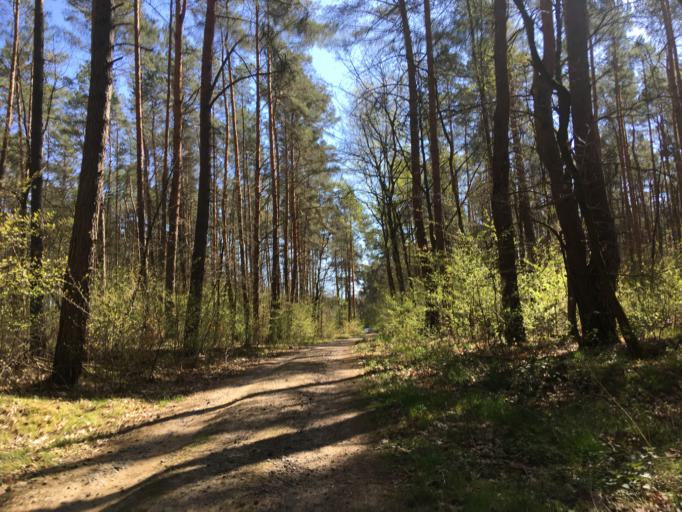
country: DE
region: Brandenburg
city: Bernau bei Berlin
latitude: 52.6993
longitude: 13.5390
